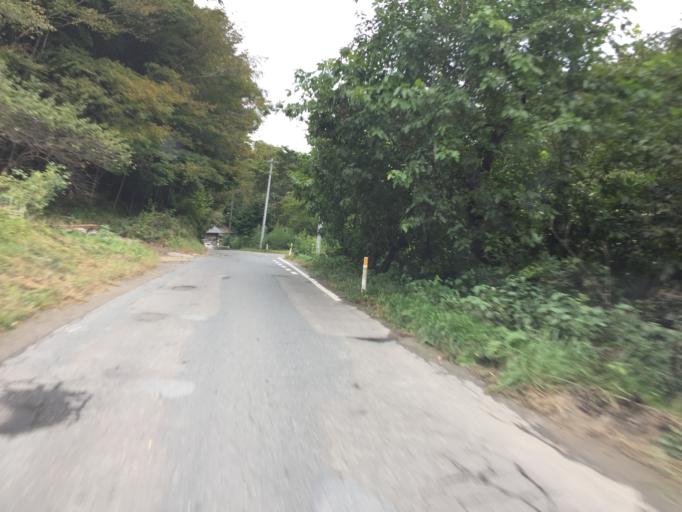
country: JP
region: Miyagi
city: Marumori
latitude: 37.9000
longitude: 140.7417
